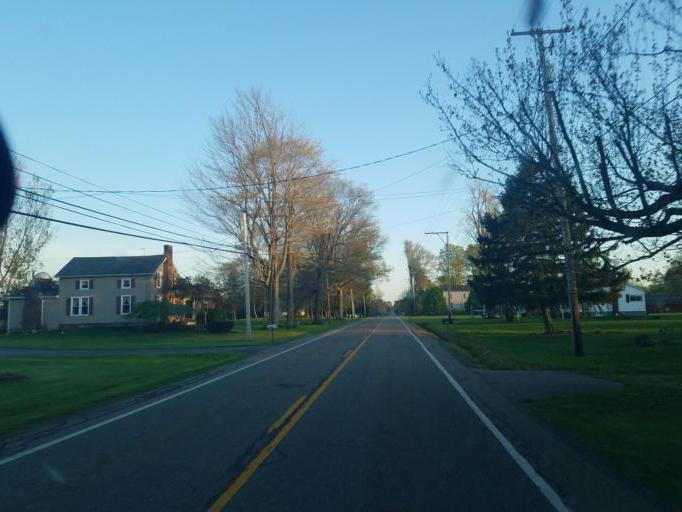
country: US
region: Ohio
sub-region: Trumbull County
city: Brookfield Center
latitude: 41.3637
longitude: -80.5690
